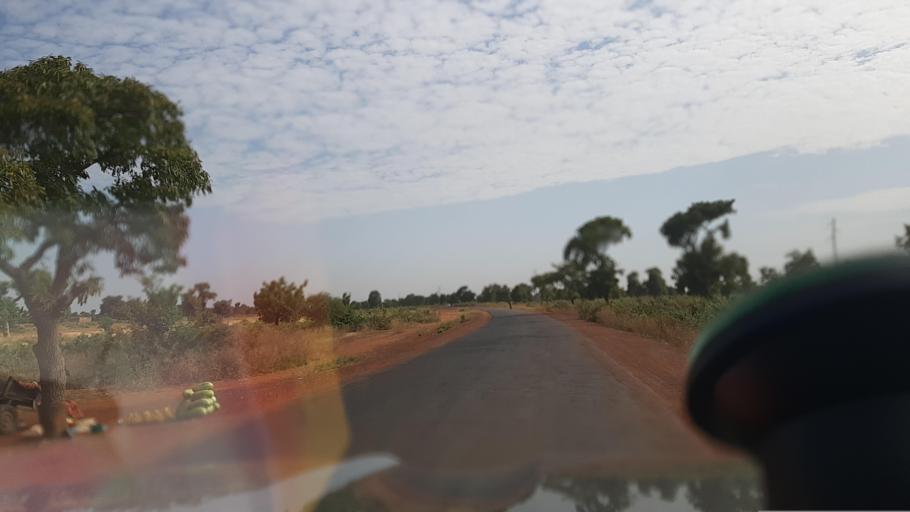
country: ML
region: Segou
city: Segou
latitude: 13.5004
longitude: -6.1518
